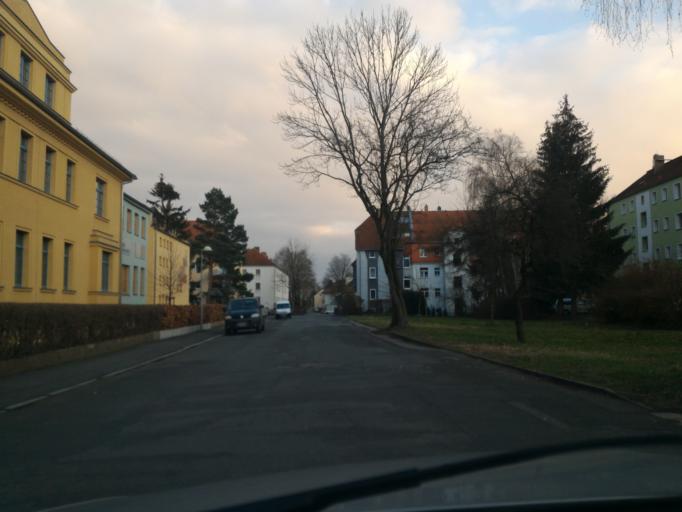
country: DE
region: Saxony
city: Zittau
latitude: 50.8923
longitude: 14.7983
